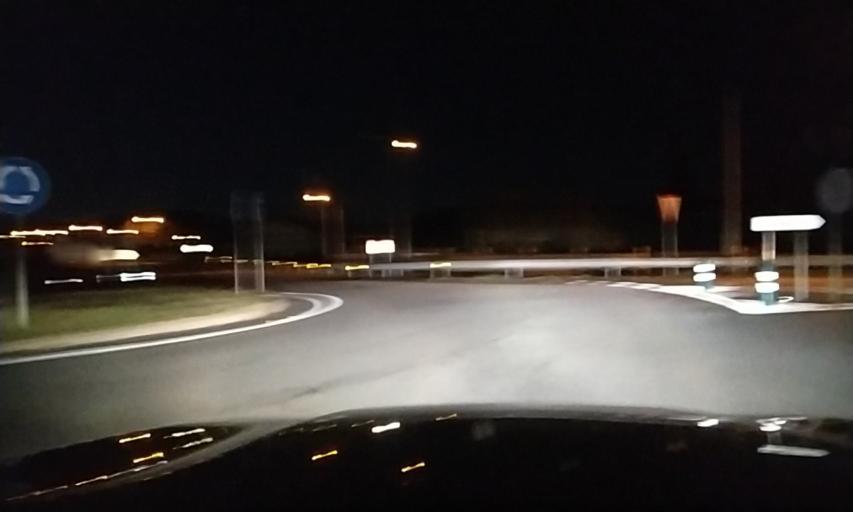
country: ES
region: Galicia
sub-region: Provincia de Ourense
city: Verin
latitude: 41.9475
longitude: -7.4892
